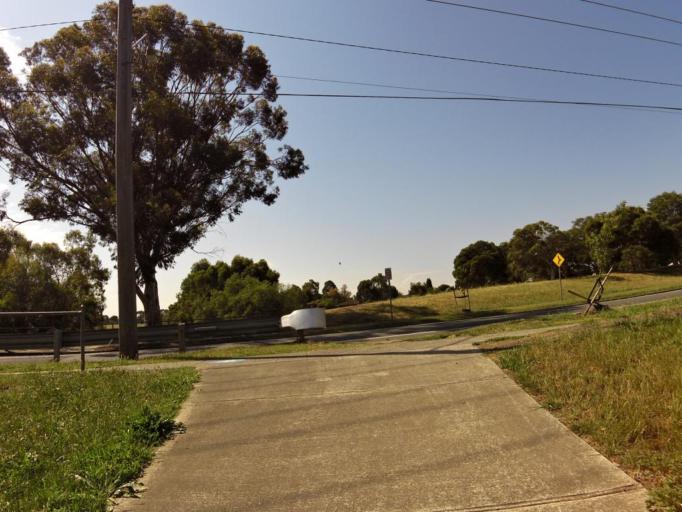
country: AU
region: Victoria
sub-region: Whittlesea
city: Epping
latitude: -37.6489
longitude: 145.0338
